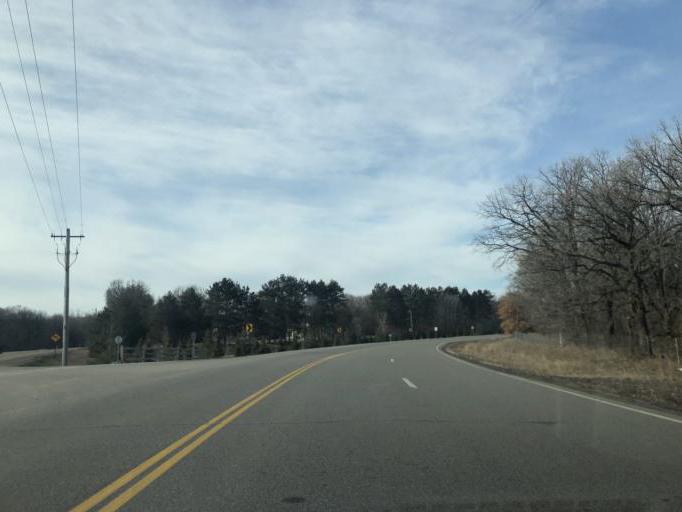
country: US
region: Minnesota
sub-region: Sherburne County
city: Becker
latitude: 45.3958
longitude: -93.8499
